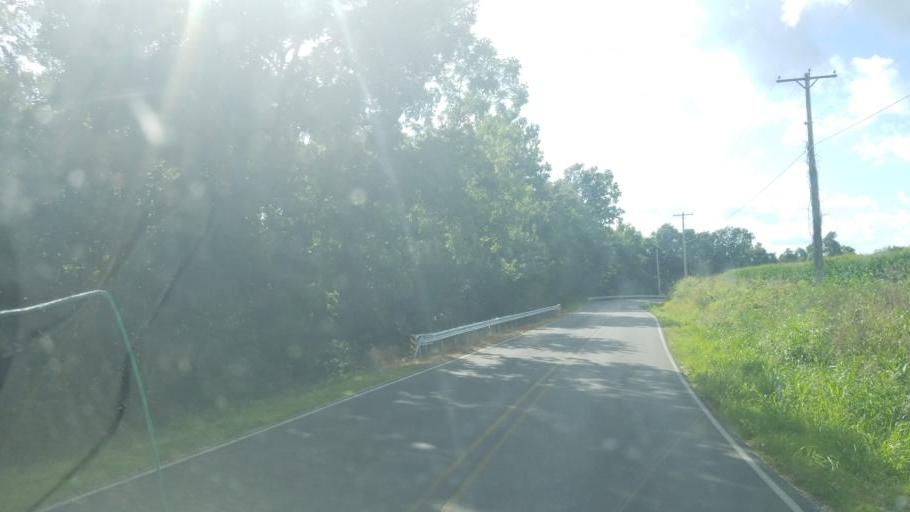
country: US
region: Illinois
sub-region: Union County
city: Cobden
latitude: 37.5620
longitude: -89.3074
